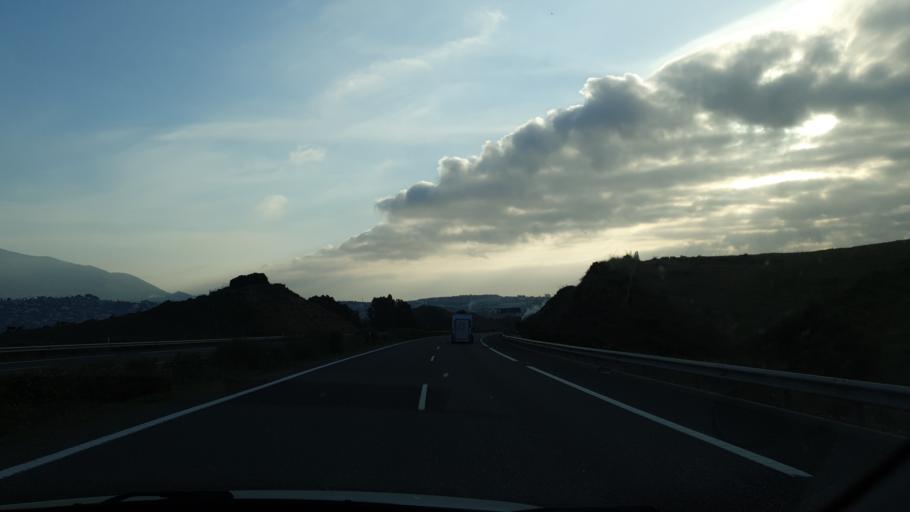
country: ES
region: Andalusia
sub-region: Provincia de Malaga
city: Fuengirola
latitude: 36.5398
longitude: -4.6738
